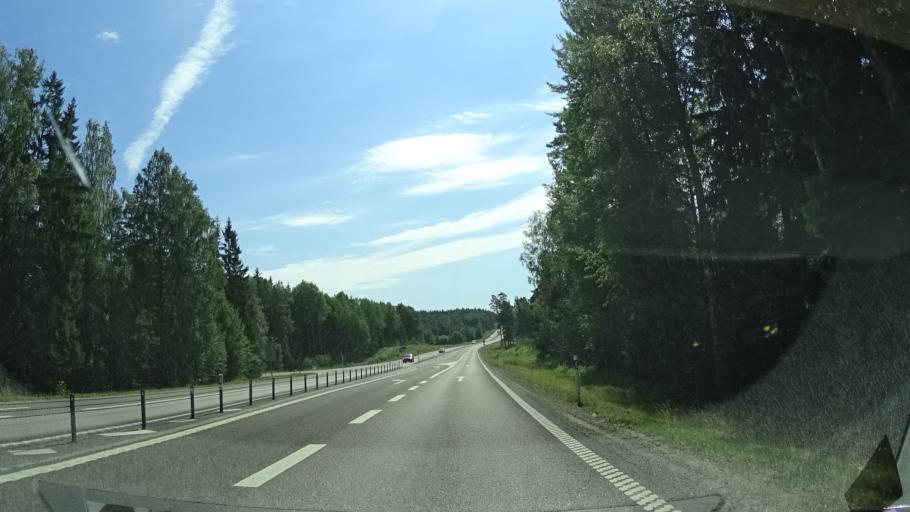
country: SE
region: Vaermland
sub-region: Kristinehamns Kommun
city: Kristinehamn
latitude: 59.3513
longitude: 14.0779
